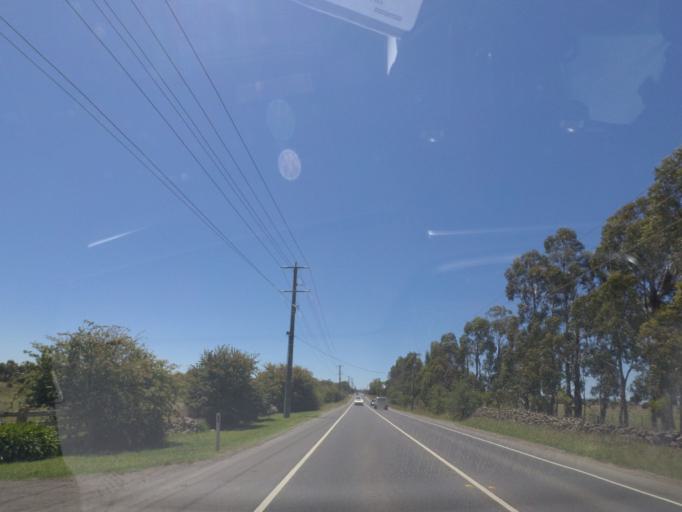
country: AU
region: Victoria
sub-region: Whittlesea
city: Epping
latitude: -37.6026
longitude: 145.0323
